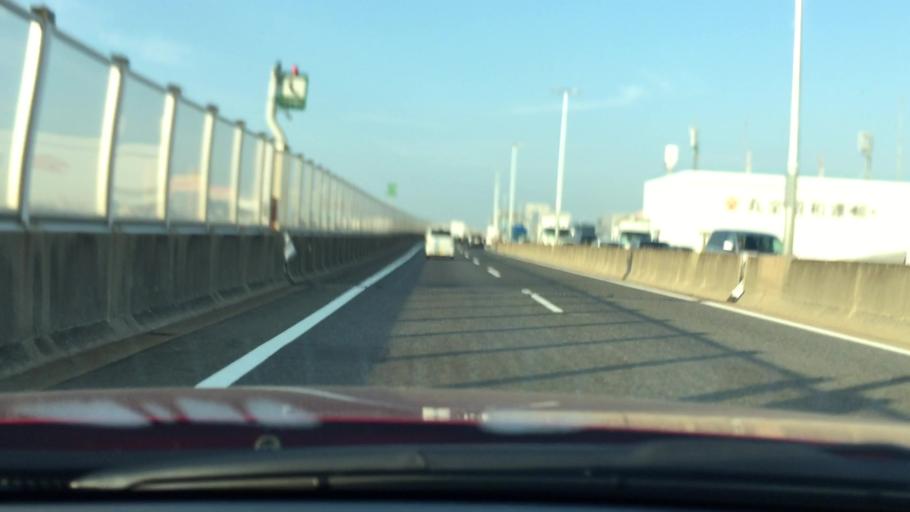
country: JP
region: Osaka
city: Takaishi
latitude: 34.5153
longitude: 135.4147
